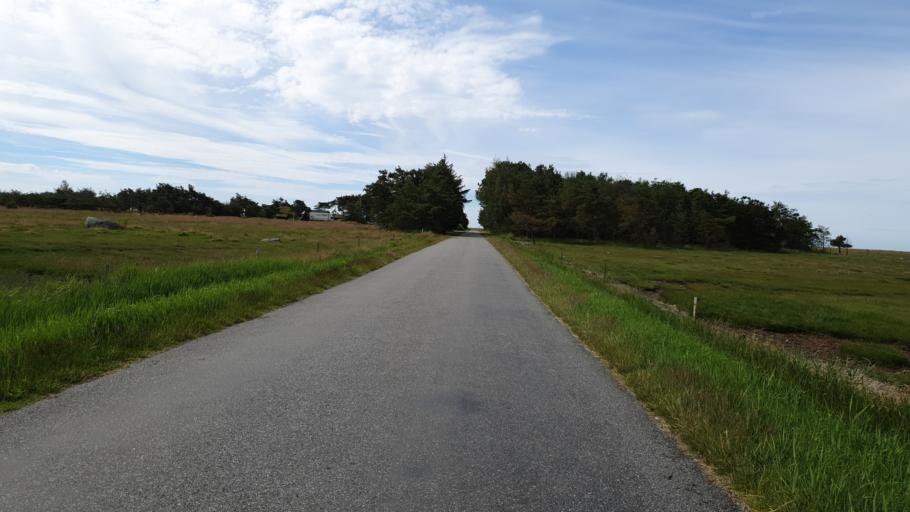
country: DK
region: North Denmark
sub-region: Laeso Kommune
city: Byrum
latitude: 57.2425
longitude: 10.9900
